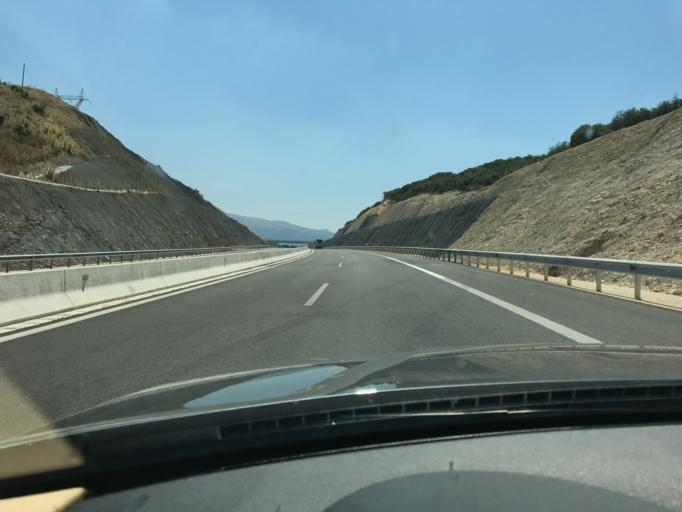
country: GR
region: Epirus
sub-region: Nomos Ioanninon
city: Agia Kyriaki
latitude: 39.4939
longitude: 20.8885
